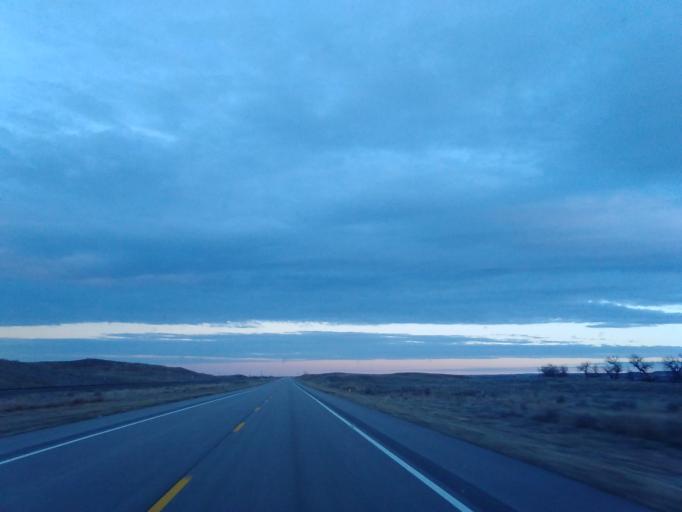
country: US
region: Nebraska
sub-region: Garden County
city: Oshkosh
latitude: 41.3780
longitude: -102.2636
